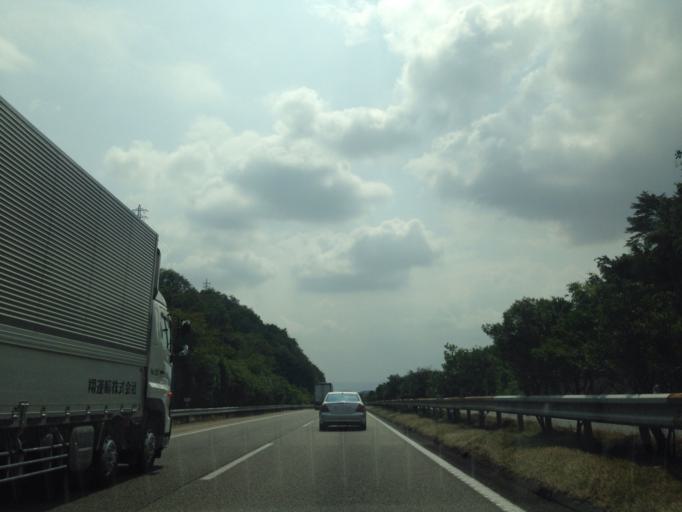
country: JP
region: Aichi
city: Kozakai-cho
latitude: 34.8591
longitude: 137.3269
